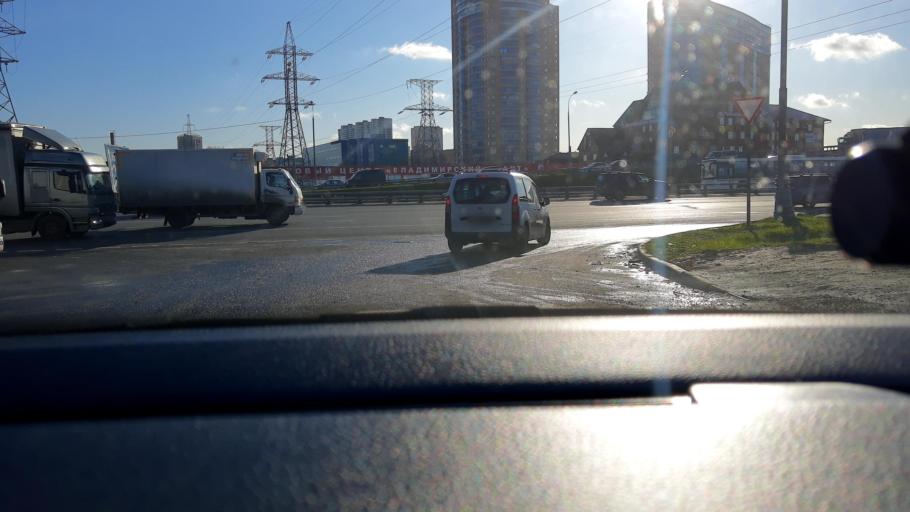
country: RU
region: Moscow
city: Ivanovskoye
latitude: 55.7786
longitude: 37.8476
